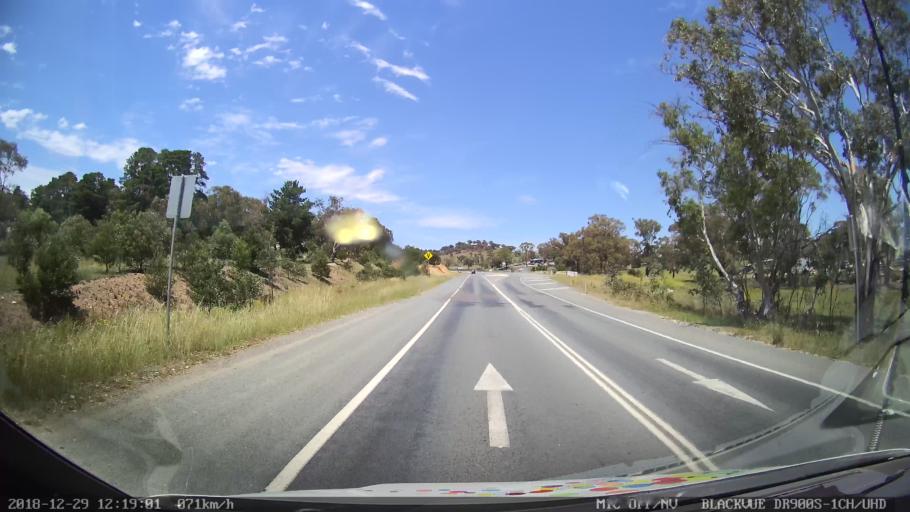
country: AU
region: New South Wales
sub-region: Queanbeyan
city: Queanbeyan
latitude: -35.3895
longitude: 149.2345
